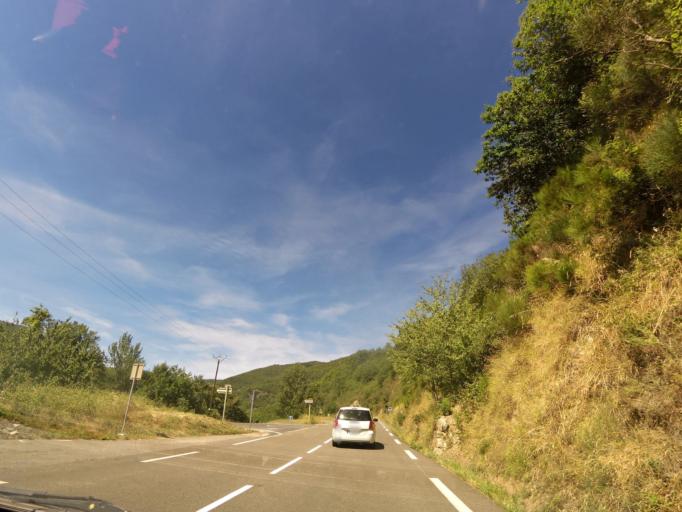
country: FR
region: Languedoc-Roussillon
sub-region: Departement du Gard
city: Le Vigan
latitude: 43.9785
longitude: 3.4821
